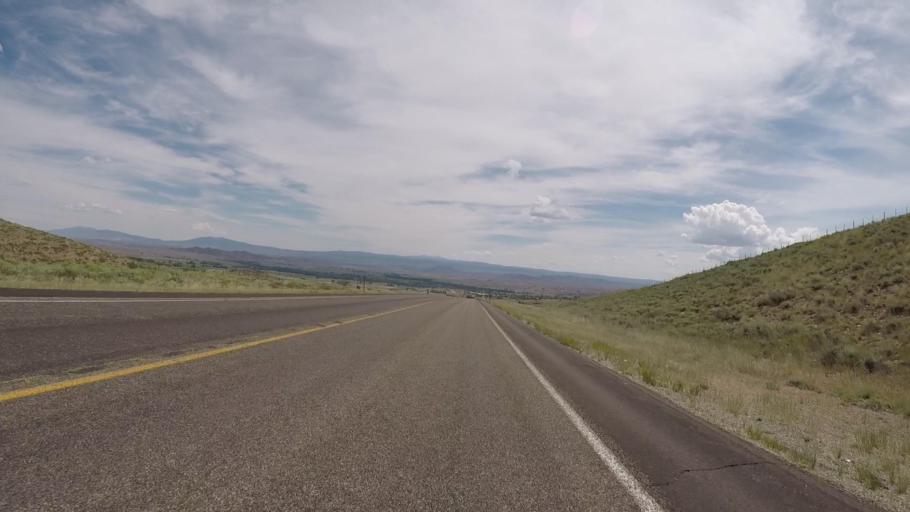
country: US
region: Wyoming
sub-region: Carbon County
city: Saratoga
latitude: 41.2030
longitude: -106.8254
